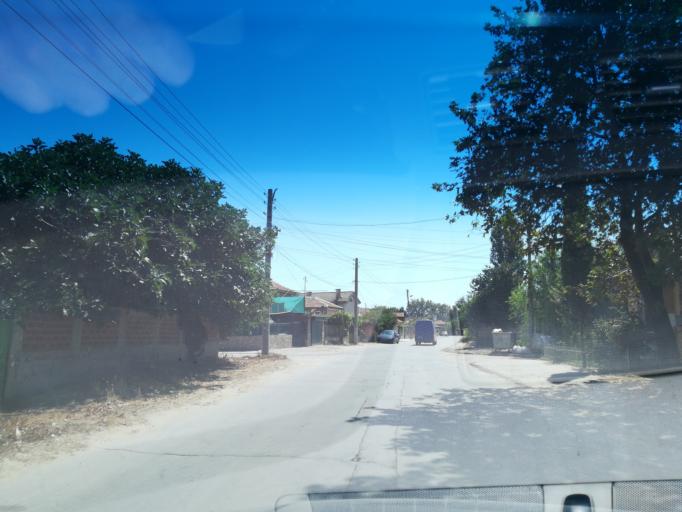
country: BG
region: Pazardzhik
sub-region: Obshtina Pazardzhik
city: Pazardzhik
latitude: 42.2751
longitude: 24.3965
